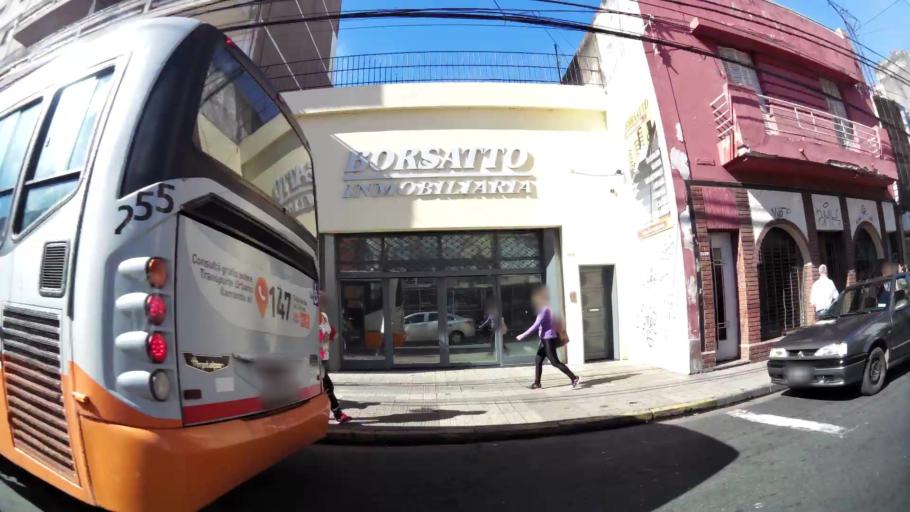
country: AR
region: Santa Fe
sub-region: Departamento de Rosario
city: Rosario
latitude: -32.9517
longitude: -60.6385
